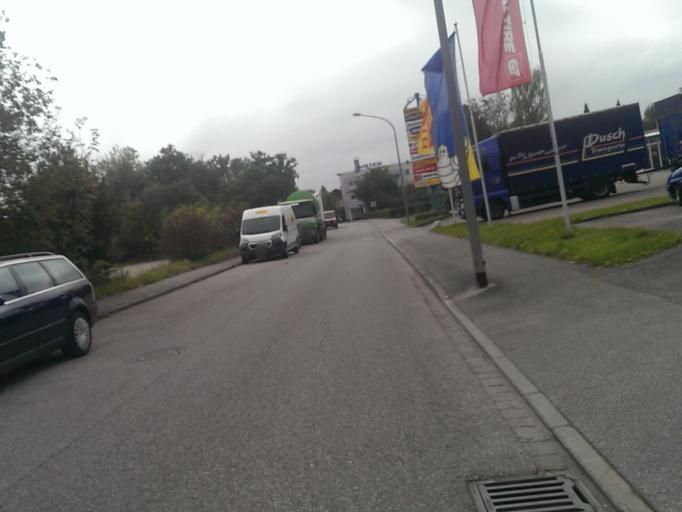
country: DE
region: Bavaria
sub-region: Upper Bavaria
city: Freilassing
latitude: 47.8364
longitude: 12.9744
